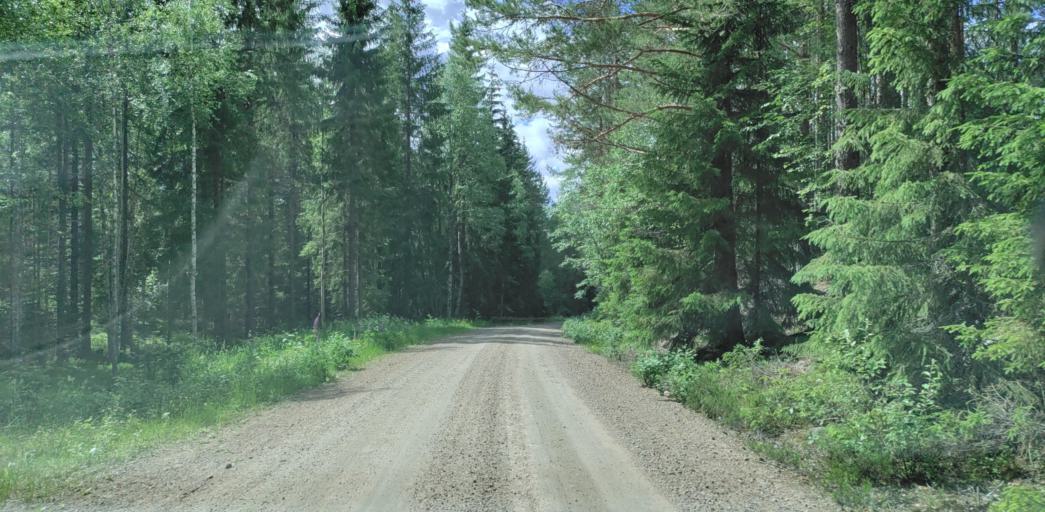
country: SE
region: Vaermland
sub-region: Hagfors Kommun
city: Ekshaerad
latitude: 60.0615
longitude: 13.2968
